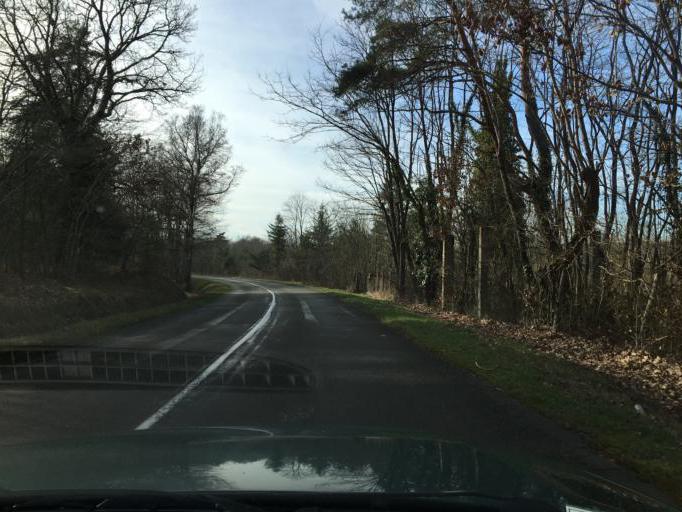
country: FR
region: Centre
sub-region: Departement du Loiret
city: La Ferte-Saint-Aubin
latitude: 47.7242
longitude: 1.9093
